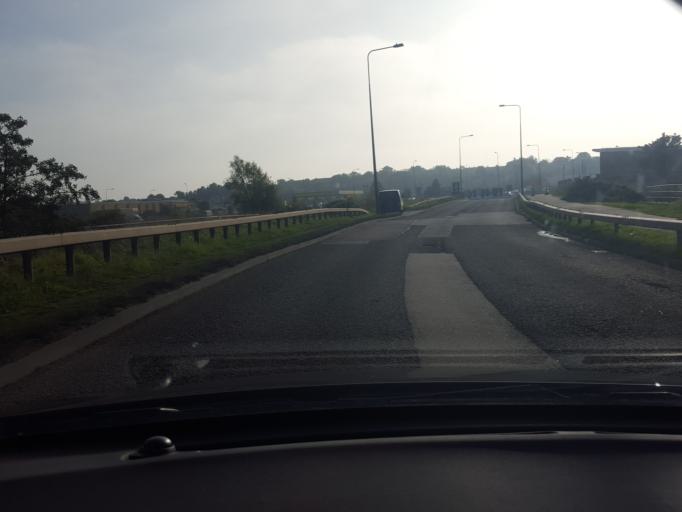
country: GB
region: England
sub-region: Suffolk
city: Shotley Gate
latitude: 51.9429
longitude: 1.2592
